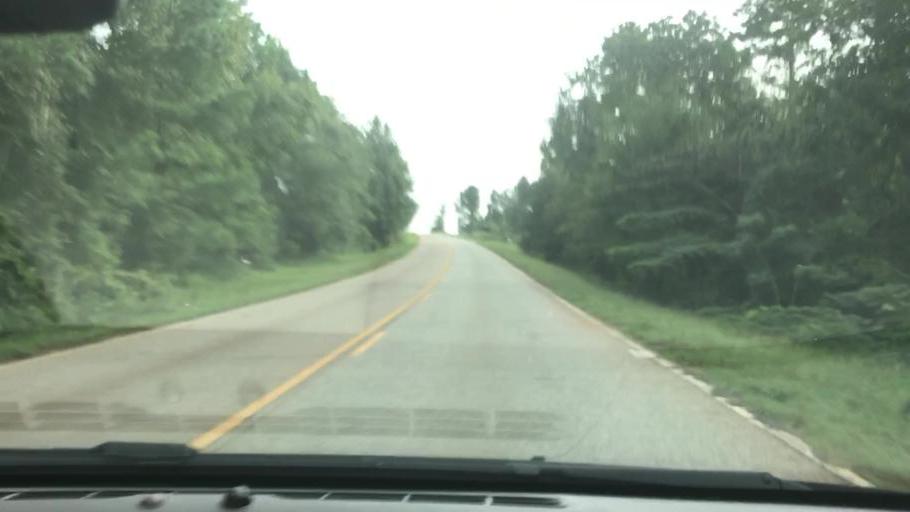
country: US
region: Georgia
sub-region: Quitman County
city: Georgetown
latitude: 31.9258
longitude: -85.0180
